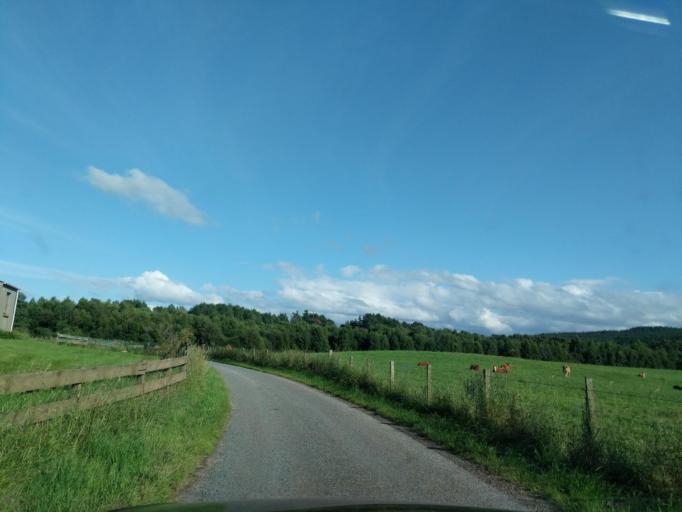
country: GB
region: Scotland
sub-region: Highland
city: Aviemore
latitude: 57.2911
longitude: -3.7515
